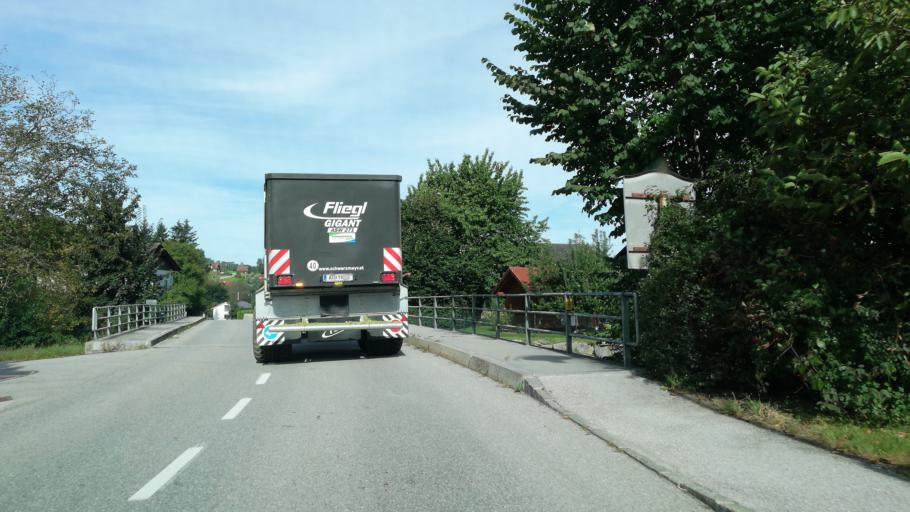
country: AT
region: Lower Austria
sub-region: Politischer Bezirk Amstetten
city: Behamberg
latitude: 48.0119
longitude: 14.4895
